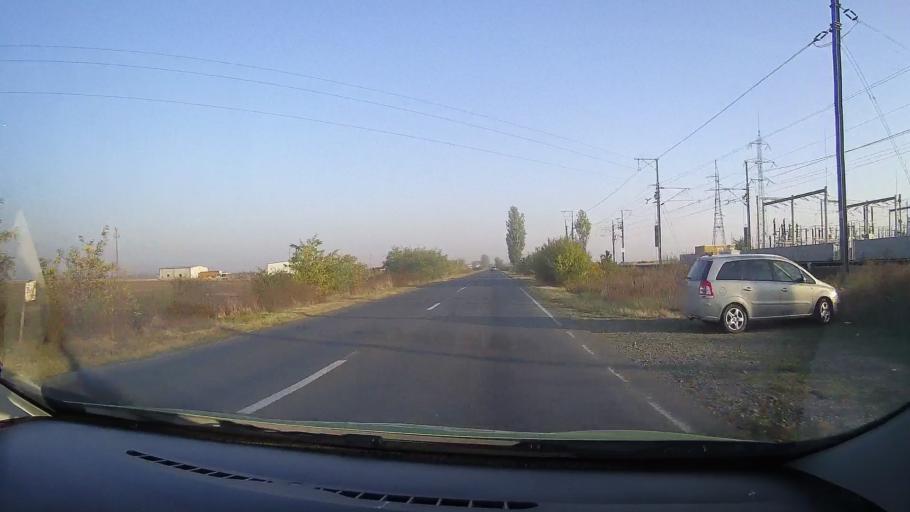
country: RO
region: Arad
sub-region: Comuna Sofronea
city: Sofronea
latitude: 46.2617
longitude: 21.3171
